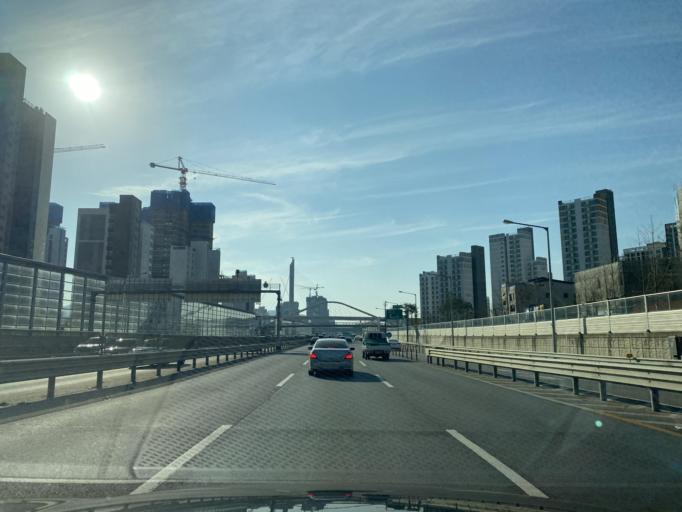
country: KR
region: Chungcheongnam-do
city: Cheonan
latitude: 36.7807
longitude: 127.0896
